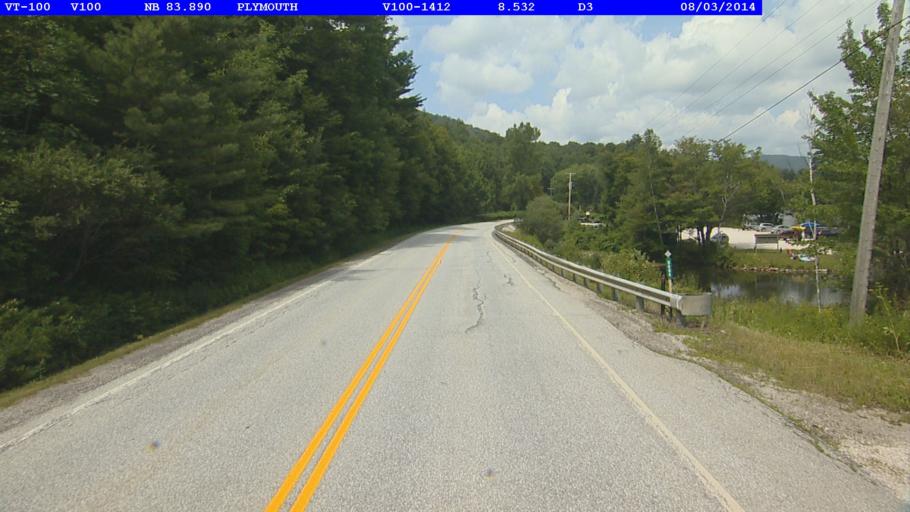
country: US
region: Vermont
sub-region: Rutland County
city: Rutland
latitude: 43.5713
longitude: -72.7625
